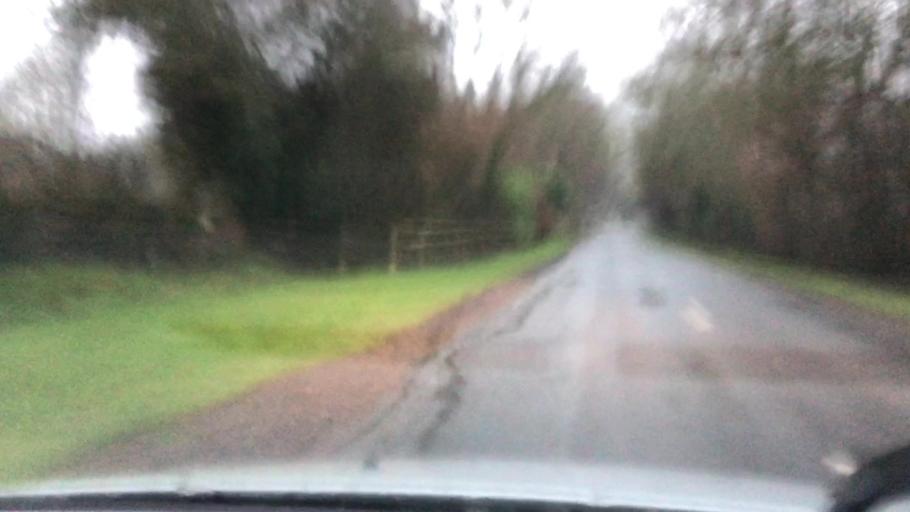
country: GB
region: England
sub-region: Hampshire
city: Alton
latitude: 51.1852
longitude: -0.9932
